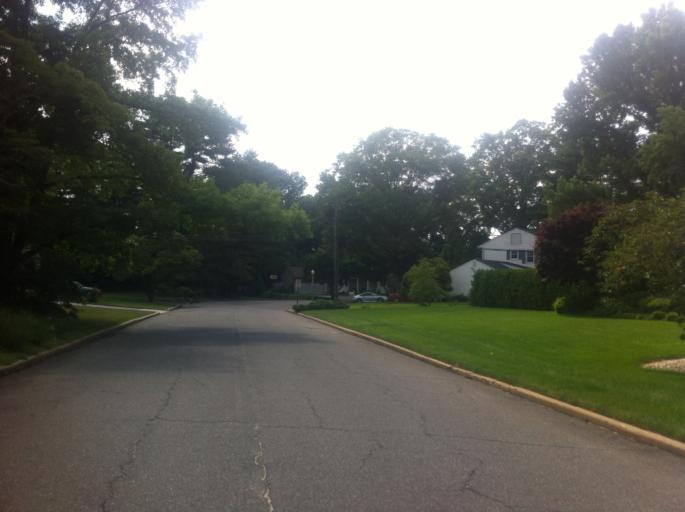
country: US
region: New York
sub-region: Nassau County
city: Locust Valley
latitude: 40.8570
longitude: -73.5992
